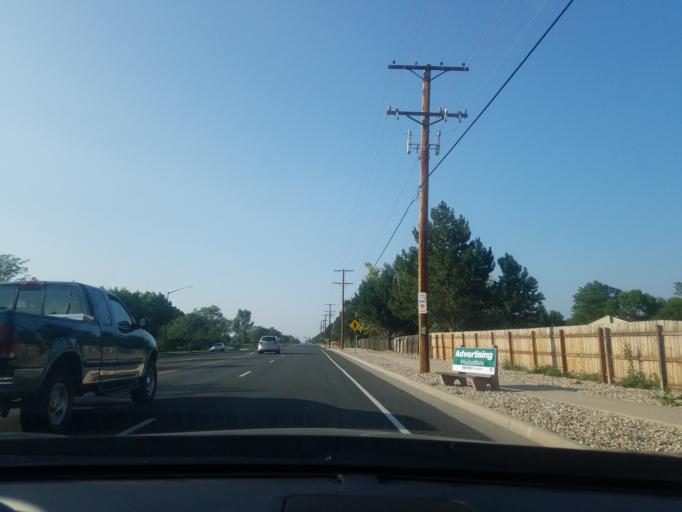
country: US
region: Colorado
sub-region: Larimer County
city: Loveland
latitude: 40.4327
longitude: -105.0965
